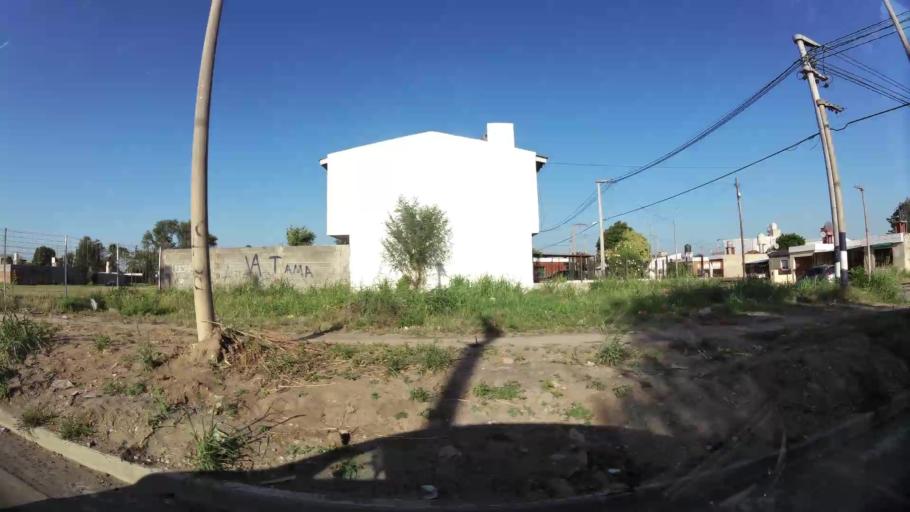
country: AR
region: Cordoba
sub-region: Departamento de Capital
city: Cordoba
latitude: -31.4420
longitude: -64.2481
